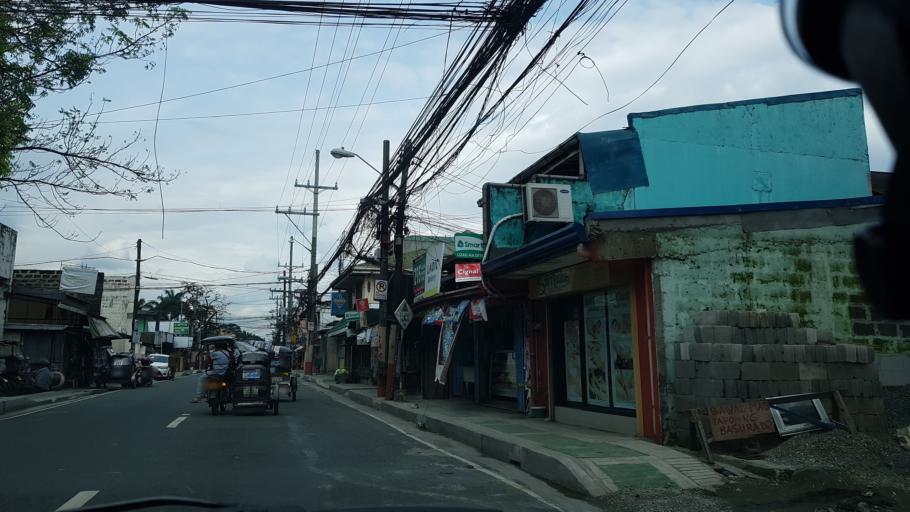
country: PH
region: Metro Manila
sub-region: Pasig
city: Pasig City
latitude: 14.5717
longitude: 121.0775
